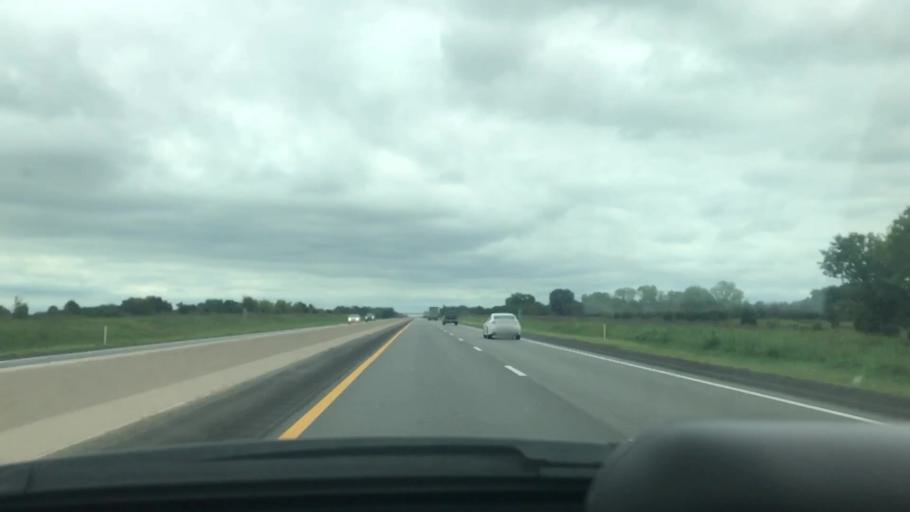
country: US
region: Oklahoma
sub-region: Craig County
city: Vinita
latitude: 36.6642
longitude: -95.0820
